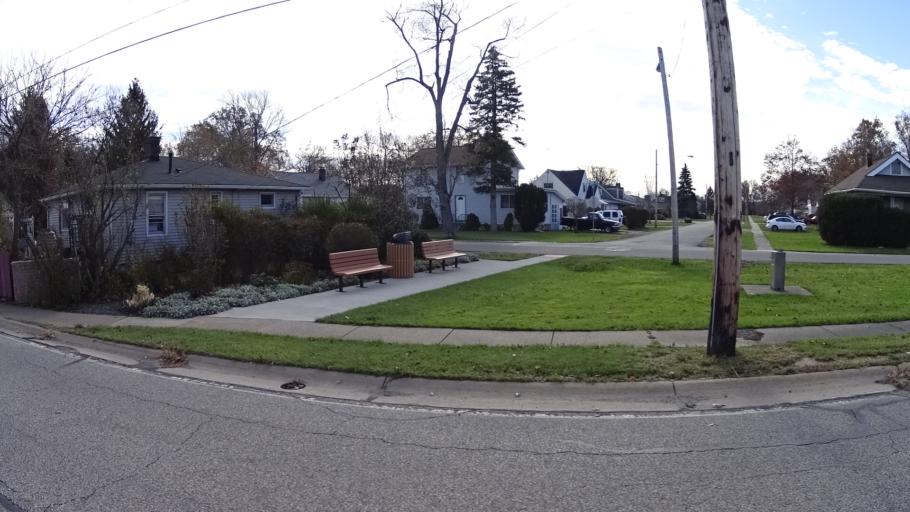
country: US
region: Ohio
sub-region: Lorain County
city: Avon Lake
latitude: 41.5040
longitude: -82.0481
